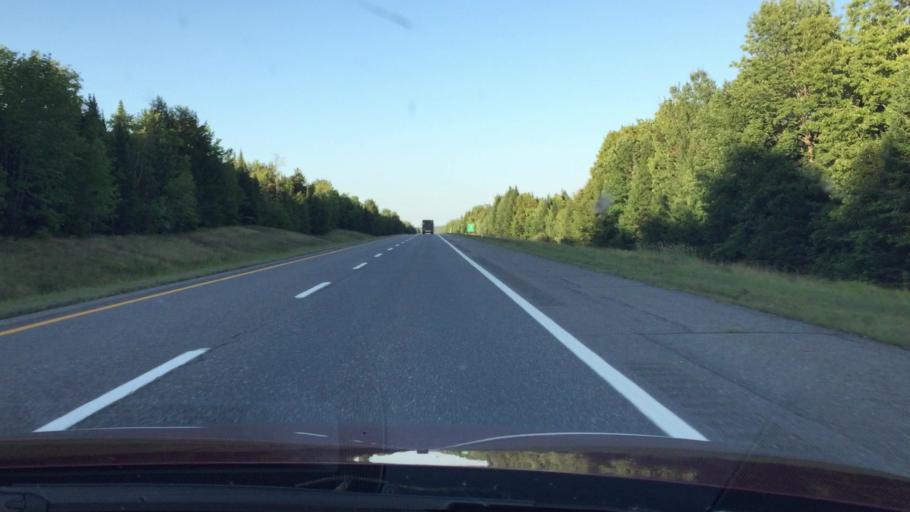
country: US
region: Maine
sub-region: Aroostook County
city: Hodgdon
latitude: 46.1254
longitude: -68.1037
